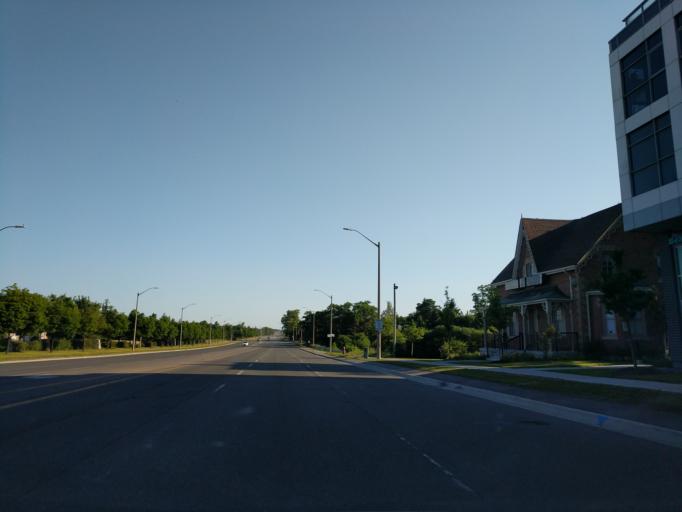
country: CA
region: Ontario
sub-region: York
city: Richmond Hill
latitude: 43.8454
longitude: -79.4078
